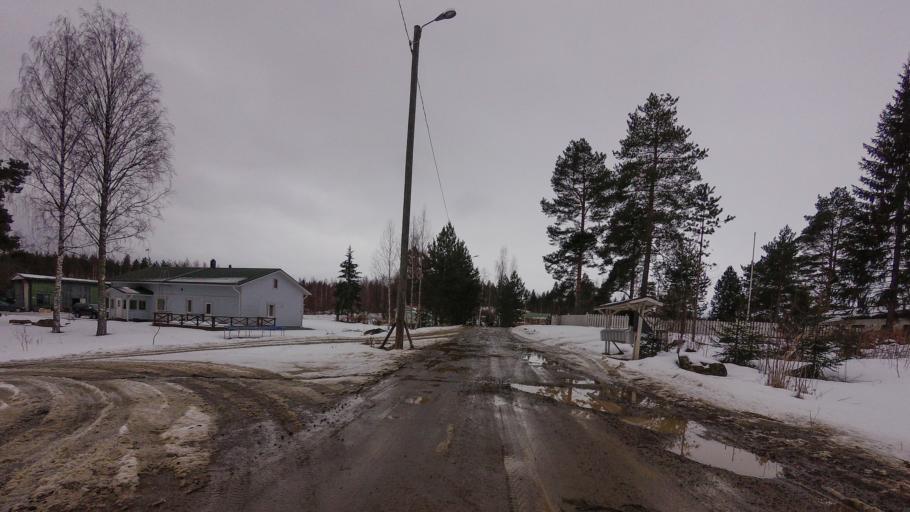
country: FI
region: Southern Savonia
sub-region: Savonlinna
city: Rantasalmi
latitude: 62.1158
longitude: 28.6098
